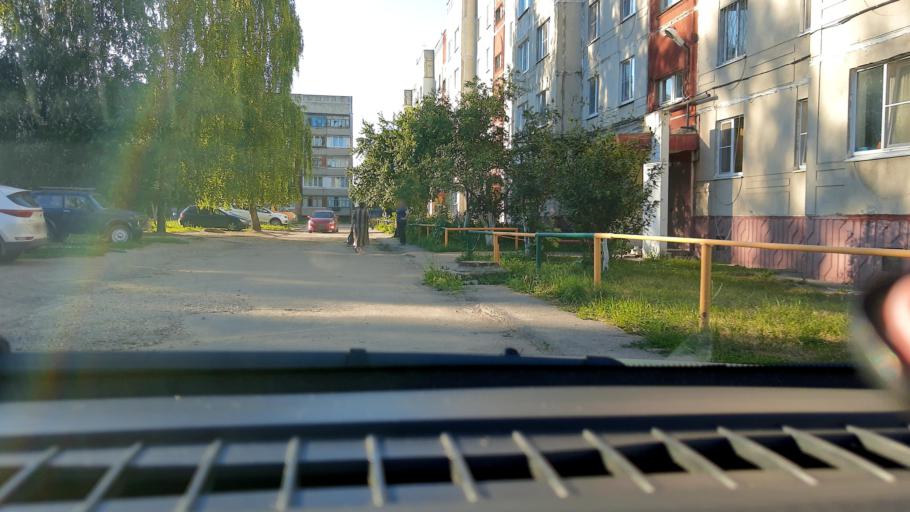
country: RU
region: Nizjnij Novgorod
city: Gorbatovka
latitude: 56.2447
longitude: 43.7485
